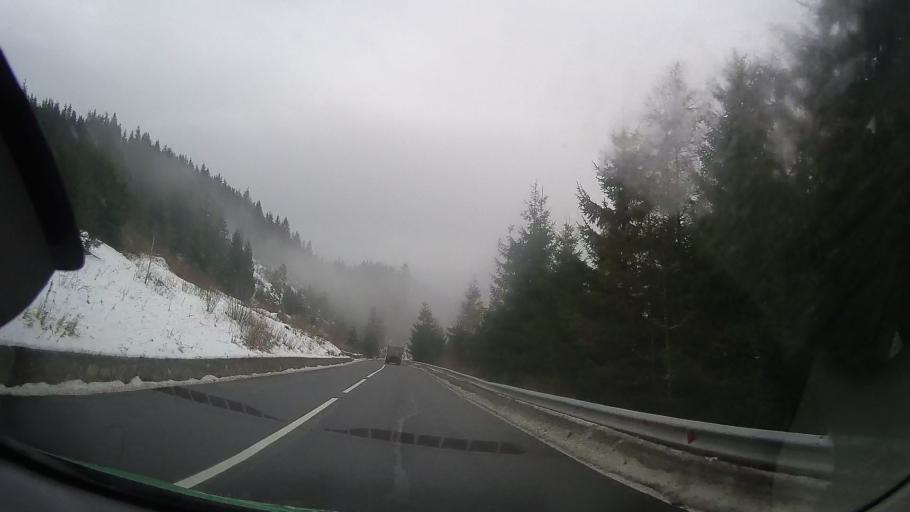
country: RO
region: Harghita
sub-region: Municipiul Gheorgheni
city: Gheorgheni
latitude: 46.7690
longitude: 25.7081
